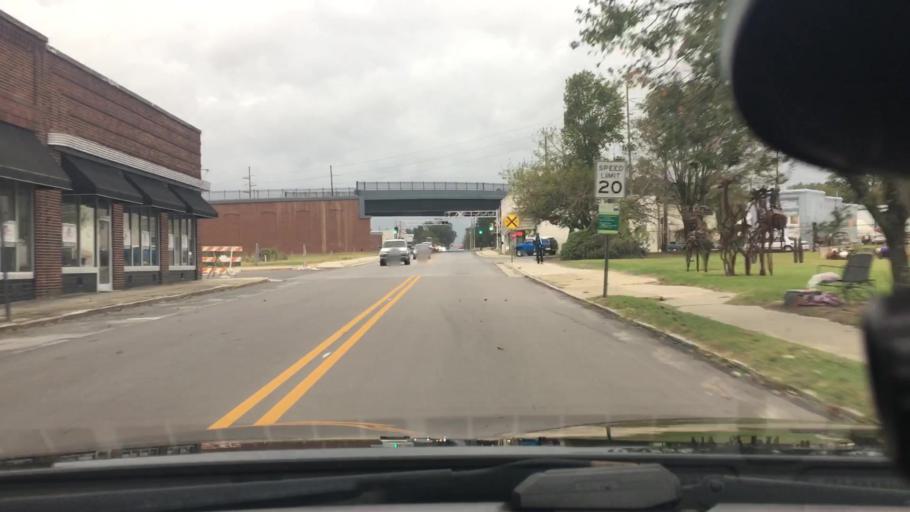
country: US
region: North Carolina
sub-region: Pitt County
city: Greenville
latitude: 35.6082
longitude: -77.3785
